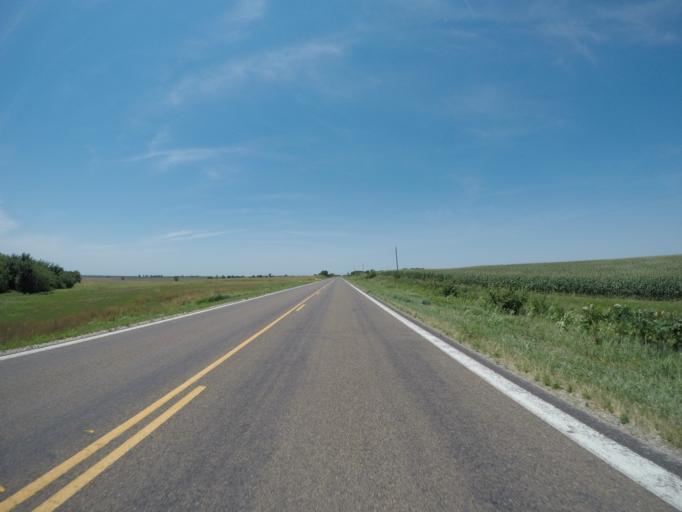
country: US
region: Kansas
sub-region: Geary County
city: Junction City
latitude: 39.0304
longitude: -96.9122
